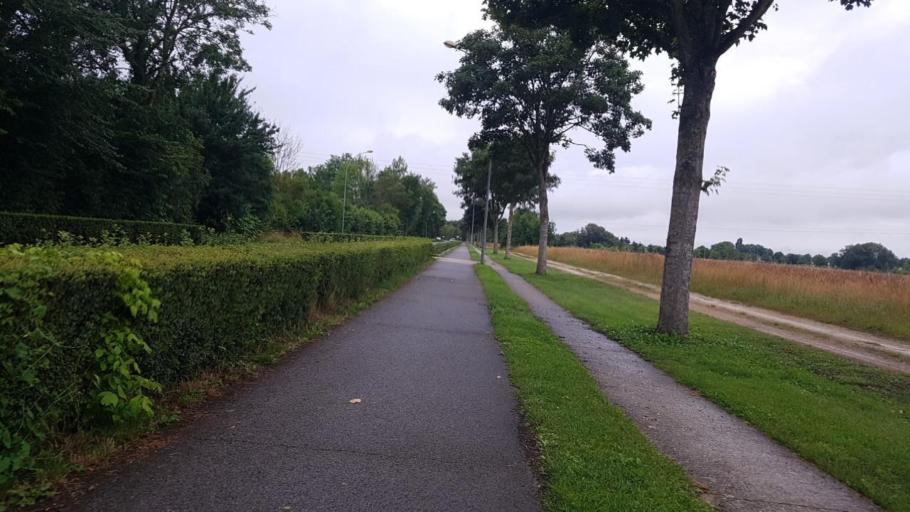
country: FR
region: Champagne-Ardenne
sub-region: Departement de la Marne
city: Sarry
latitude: 48.9301
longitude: 4.3929
